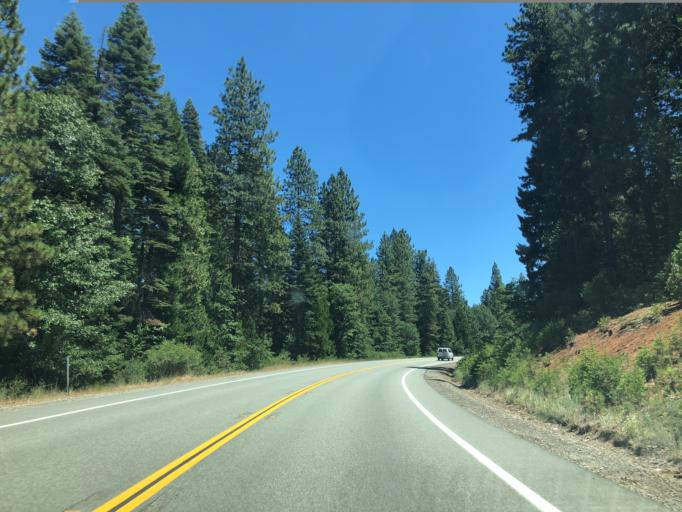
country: US
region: California
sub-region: Shasta County
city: Shingletown
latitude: 40.4927
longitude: -121.9012
